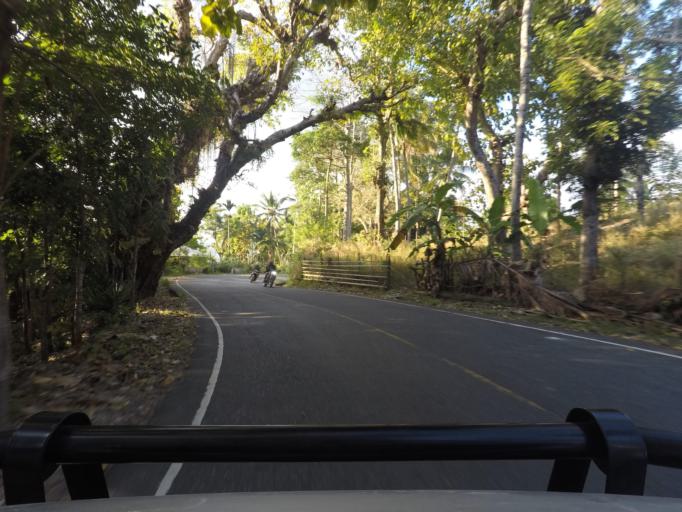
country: TL
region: Bobonaro
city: Maliana
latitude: -8.9552
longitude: 125.0788
